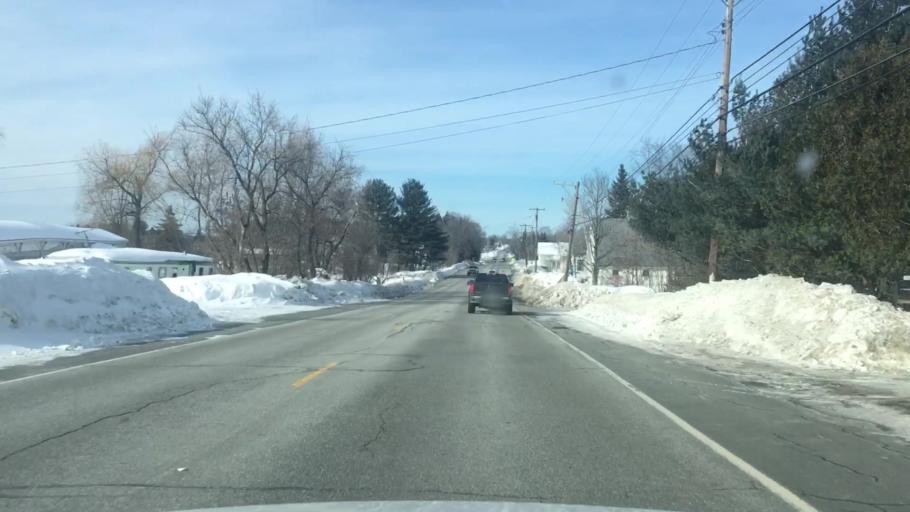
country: US
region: Maine
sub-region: Penobscot County
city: Charleston
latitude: 45.0111
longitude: -69.0263
